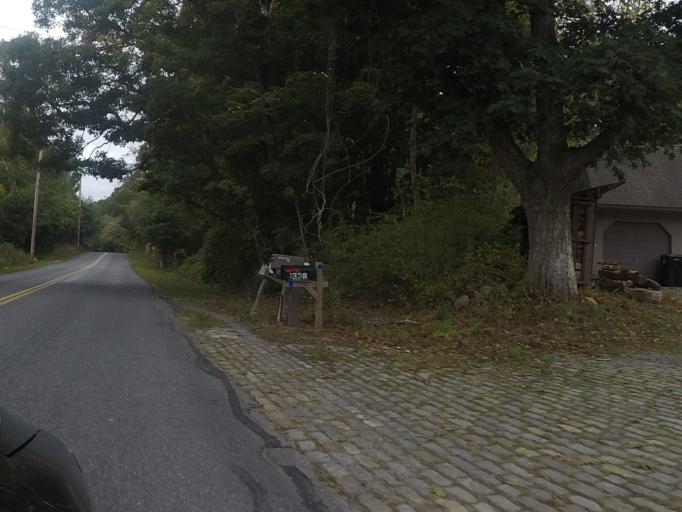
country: US
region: Massachusetts
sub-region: Bristol County
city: Smith Mills
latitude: 41.5639
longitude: -71.0071
